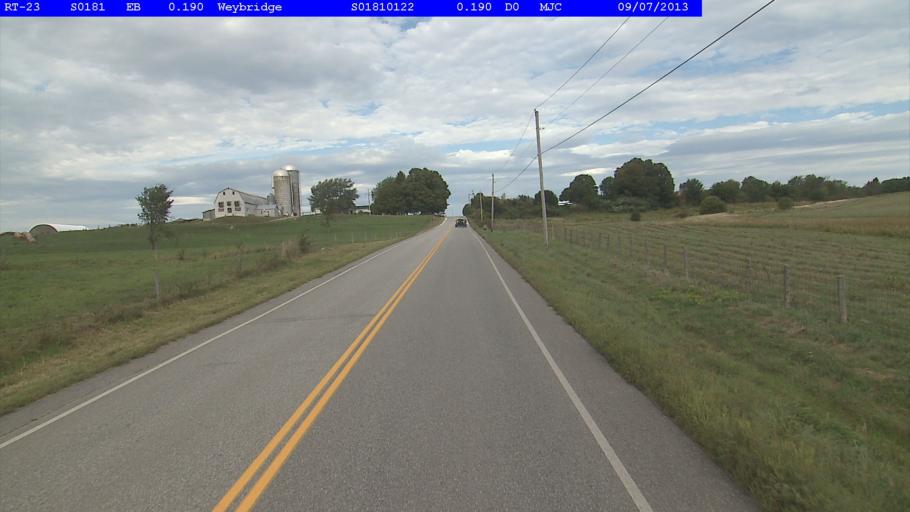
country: US
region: Vermont
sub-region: Addison County
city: Middlebury (village)
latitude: 44.0208
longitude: -73.1853
